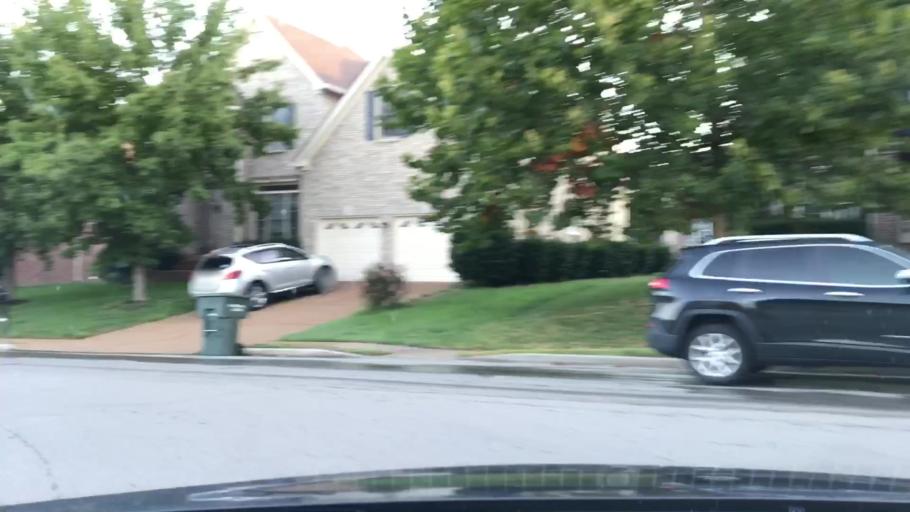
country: US
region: Tennessee
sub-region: Williamson County
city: Brentwood Estates
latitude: 36.0192
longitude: -86.7367
